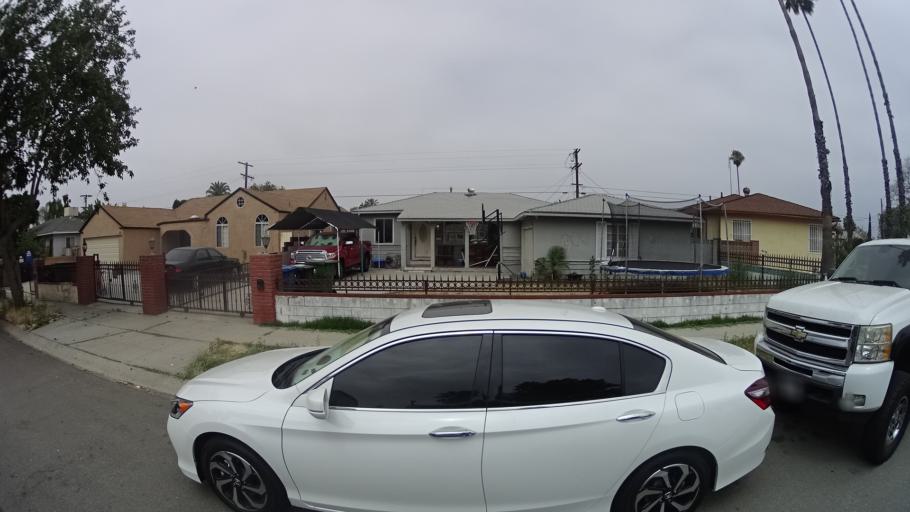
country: US
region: California
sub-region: Los Angeles County
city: North Hollywood
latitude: 34.1918
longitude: -118.4072
